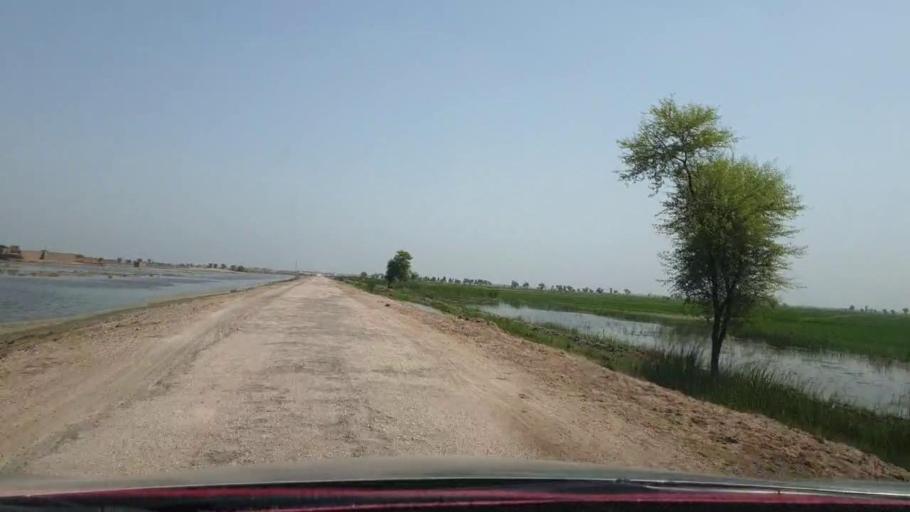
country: PK
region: Sindh
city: Warah
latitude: 27.3798
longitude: 67.7875
